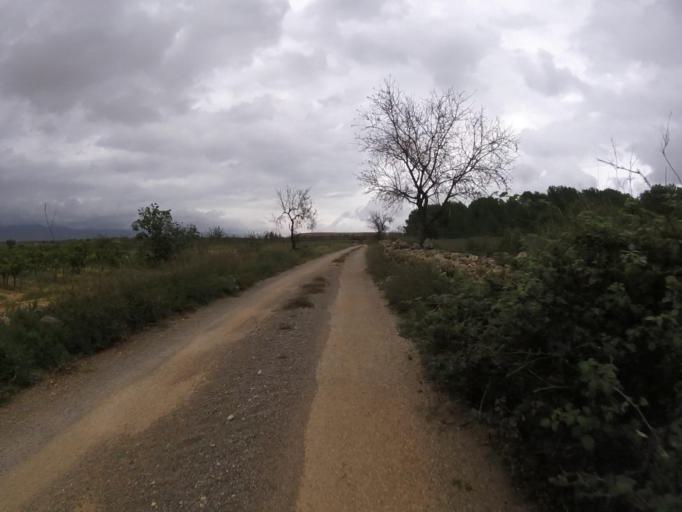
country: ES
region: Valencia
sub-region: Provincia de Castello
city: Benlloch
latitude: 40.1985
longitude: 0.0550
